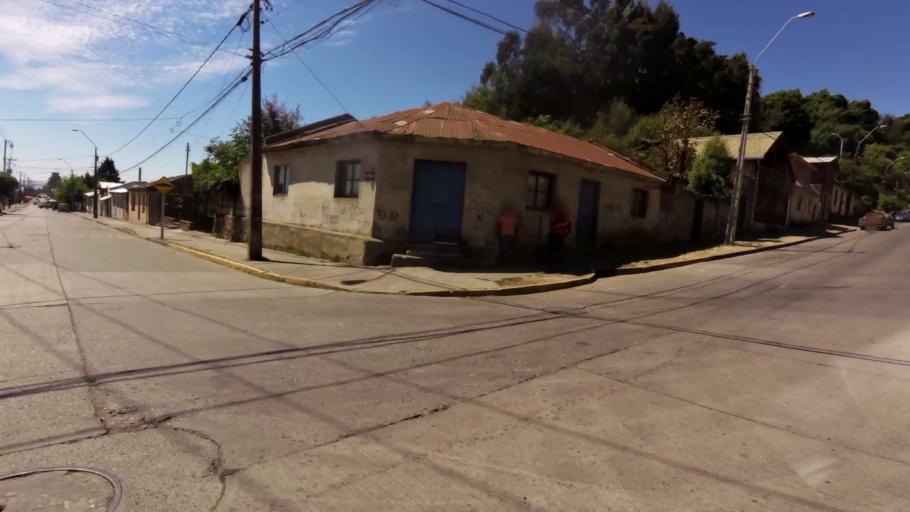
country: CL
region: Biobio
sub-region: Provincia de Concepcion
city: Penco
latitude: -36.7407
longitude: -72.9903
